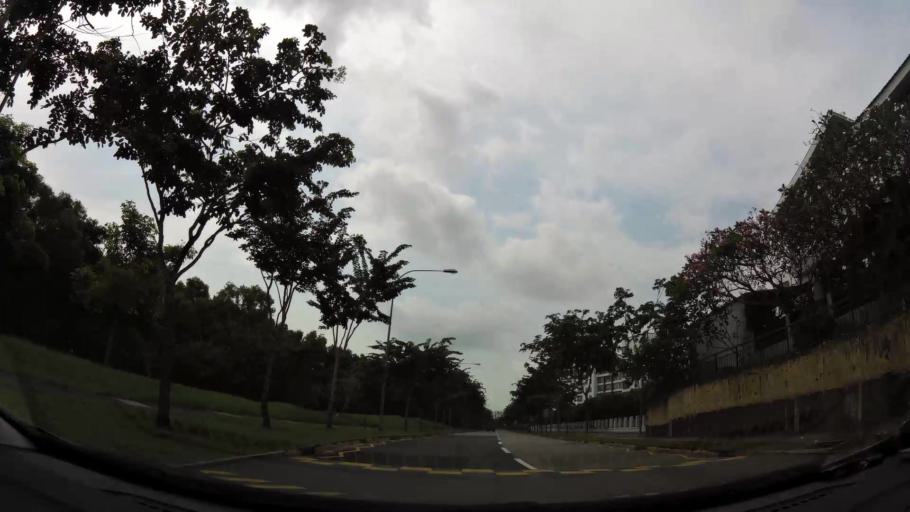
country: SG
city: Singapore
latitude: 1.3586
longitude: 103.9761
